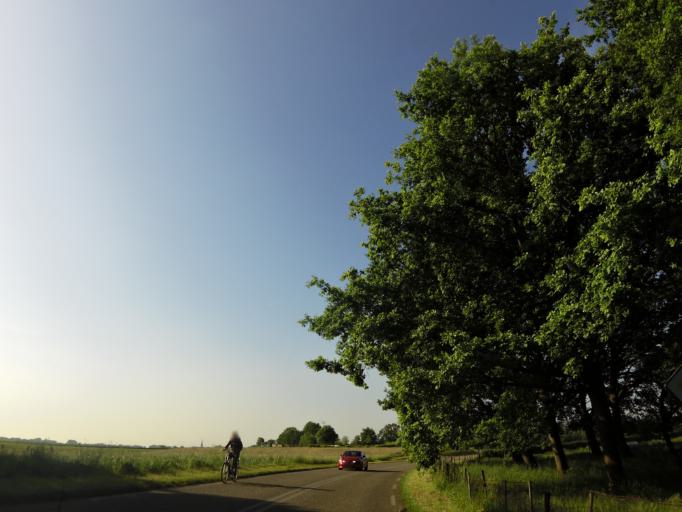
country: NL
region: Limburg
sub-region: Gemeente Beek
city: Beek
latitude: 50.9256
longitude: 5.8076
